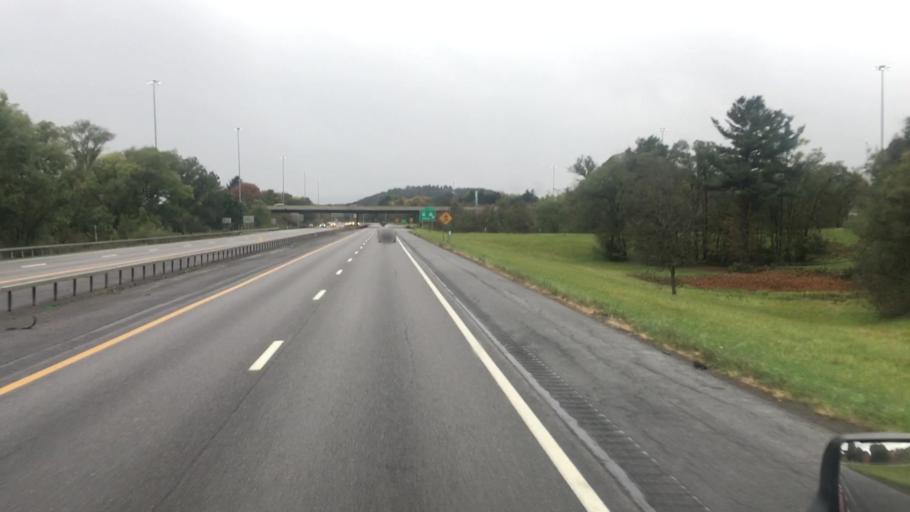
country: US
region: New York
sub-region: Broome County
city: Endicott
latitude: 42.0925
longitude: -76.0396
